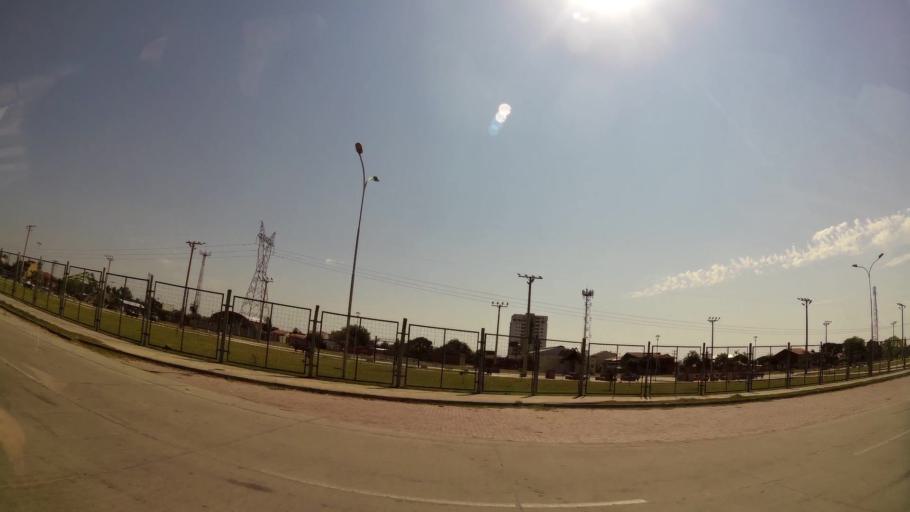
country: BO
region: Santa Cruz
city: Santa Cruz de la Sierra
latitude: -17.7417
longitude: -63.1445
